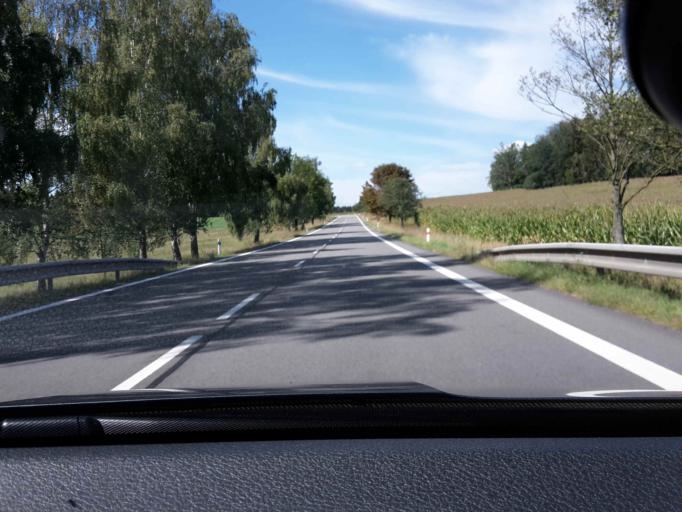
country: CZ
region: Jihocesky
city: Strmilov
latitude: 49.1769
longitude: 15.1532
